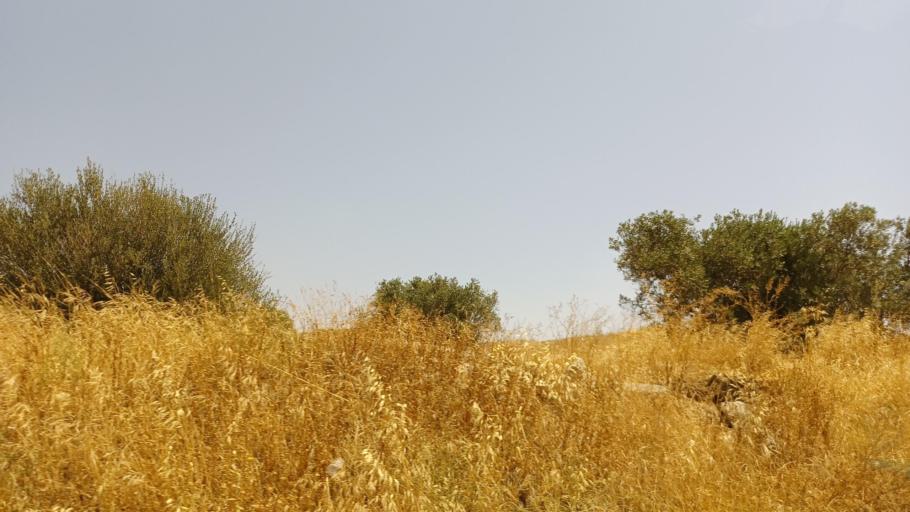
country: CY
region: Larnaka
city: Troulloi
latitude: 35.0329
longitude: 33.6346
